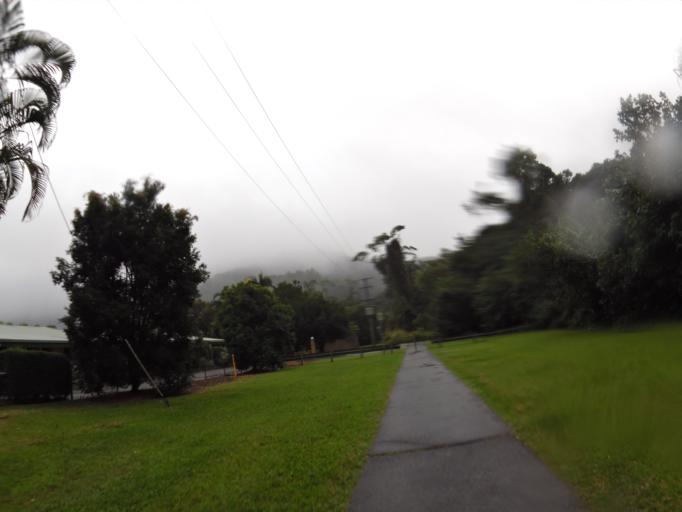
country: AU
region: Queensland
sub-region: Cairns
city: Cairns
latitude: -16.9022
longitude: 145.7462
